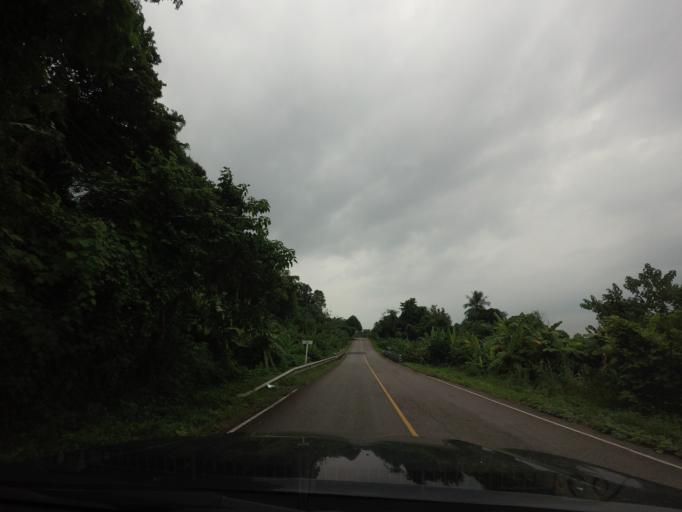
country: TH
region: Nong Khai
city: Sangkhom
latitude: 18.0456
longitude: 102.3249
